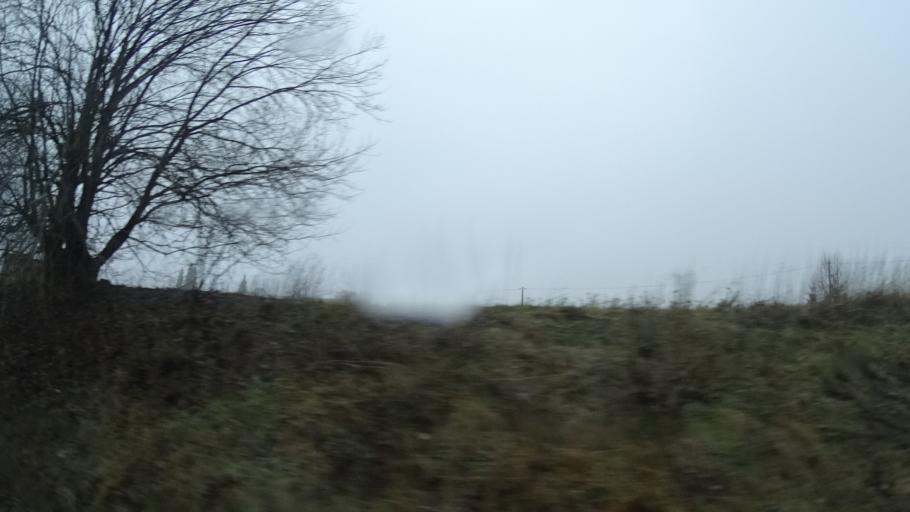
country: DE
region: Thuringia
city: Eisfeld
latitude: 50.4999
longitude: 10.9029
